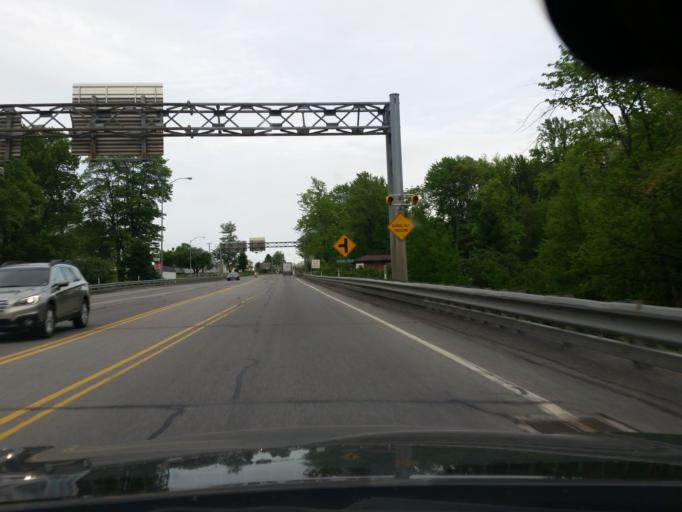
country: US
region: Pennsylvania
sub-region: Elk County
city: Ridgway
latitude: 41.4115
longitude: -78.7127
